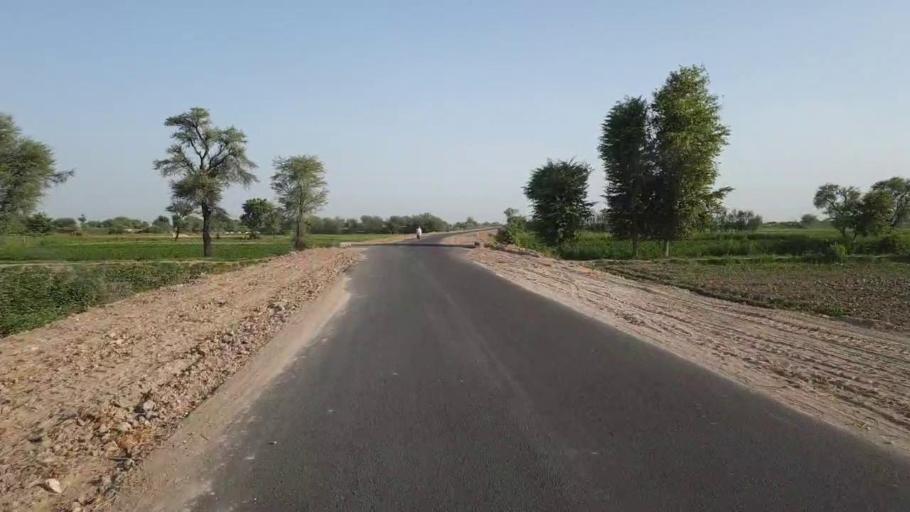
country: PK
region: Sindh
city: Jam Sahib
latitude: 26.3398
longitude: 68.5727
